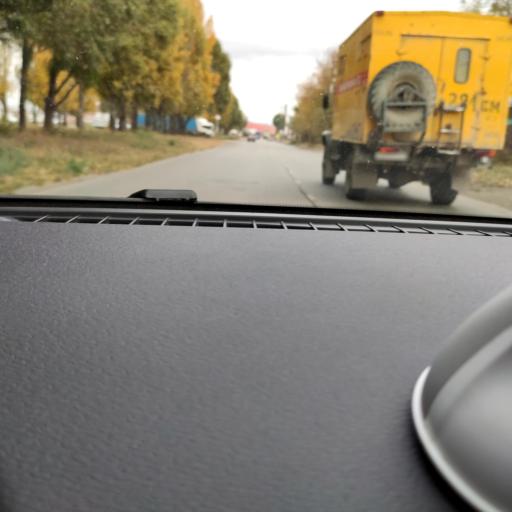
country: RU
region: Samara
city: Petra-Dubrava
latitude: 53.2499
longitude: 50.3101
